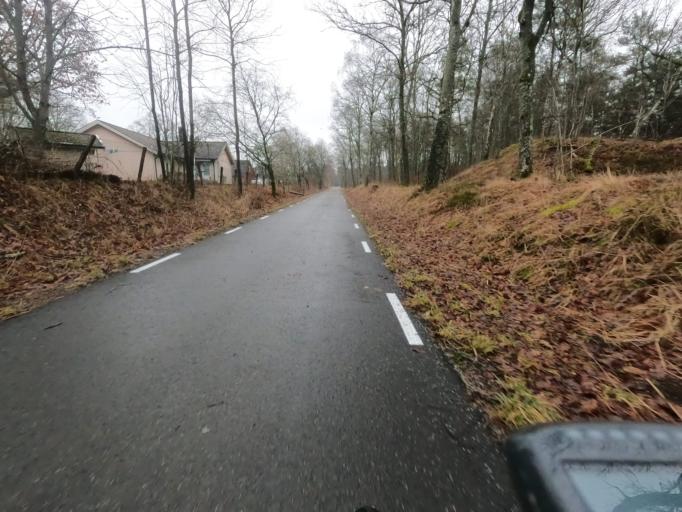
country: SE
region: Halland
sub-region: Halmstads Kommun
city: Aled
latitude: 56.6953
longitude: 12.9974
